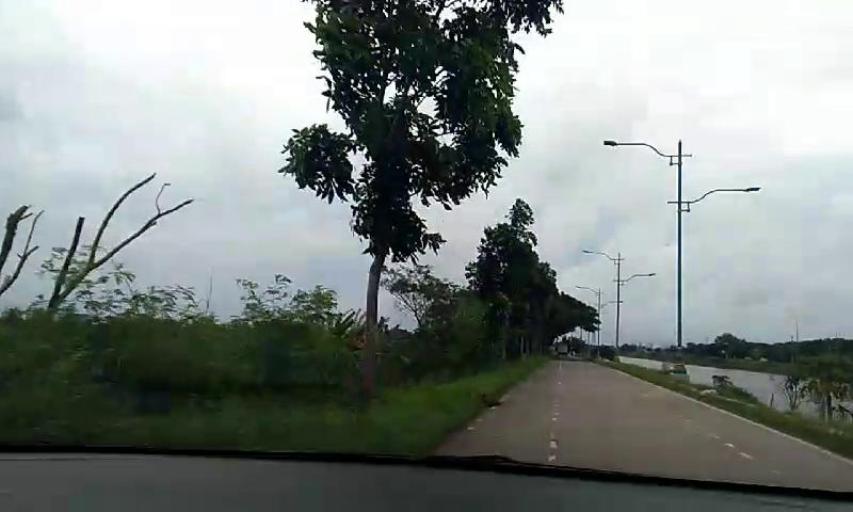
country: ID
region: West Java
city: Bekasi
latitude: -6.1280
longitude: 106.9691
